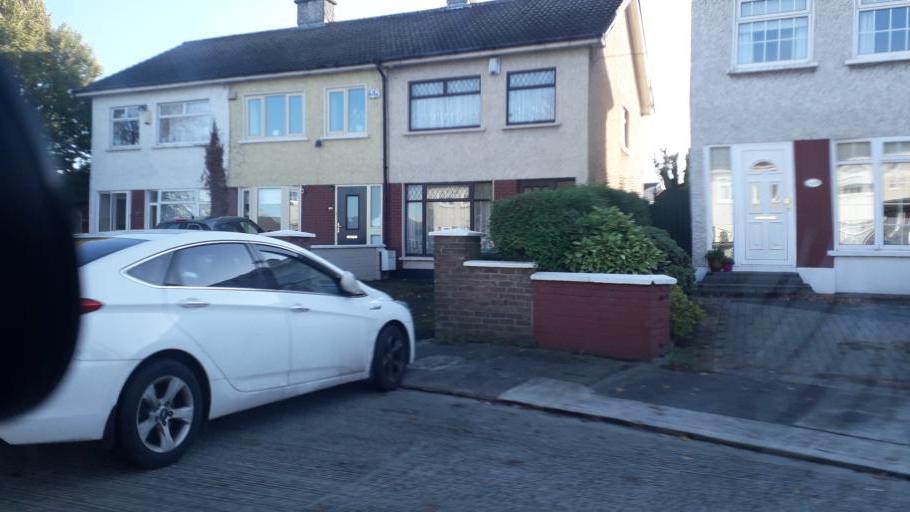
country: IE
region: Leinster
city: Artane
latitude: 53.3860
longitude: -6.2194
